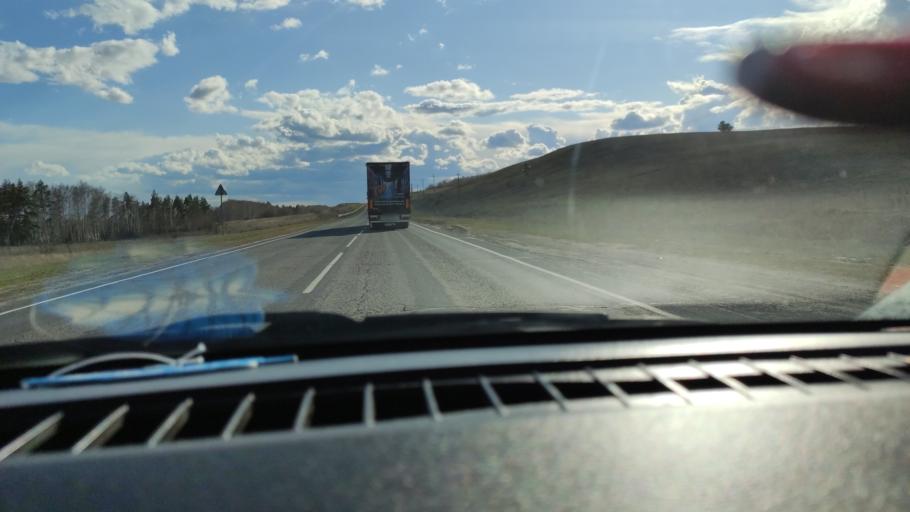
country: RU
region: Saratov
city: Sinodskoye
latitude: 52.0732
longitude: 46.7822
